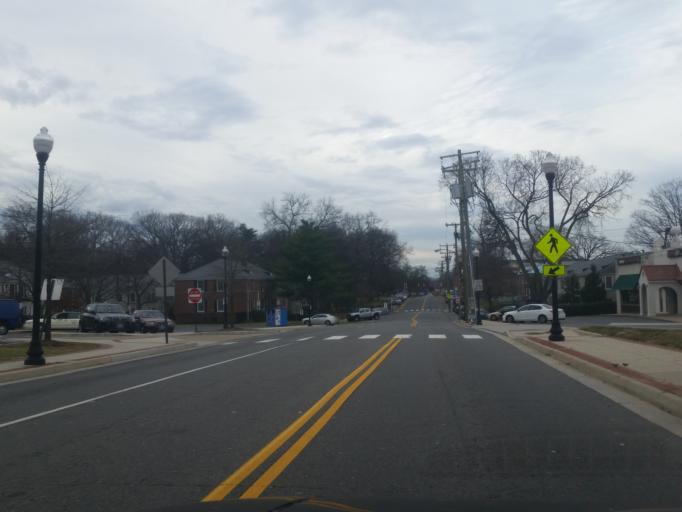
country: US
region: Virginia
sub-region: Arlington County
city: Arlington
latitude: 38.8737
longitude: -77.1055
